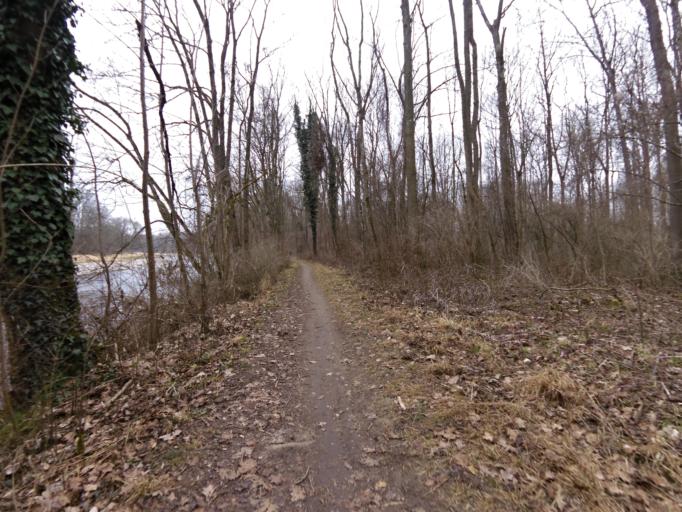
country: DE
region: Bavaria
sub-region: Upper Bavaria
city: Wang
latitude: 48.4968
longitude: 11.9512
